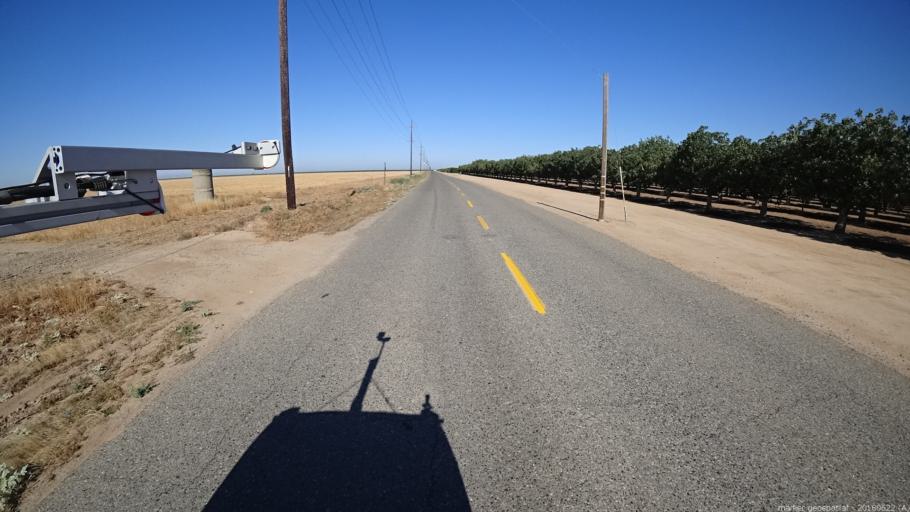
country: US
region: California
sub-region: Madera County
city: Bonadelle Ranchos-Madera Ranchos
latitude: 36.8955
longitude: -119.8018
